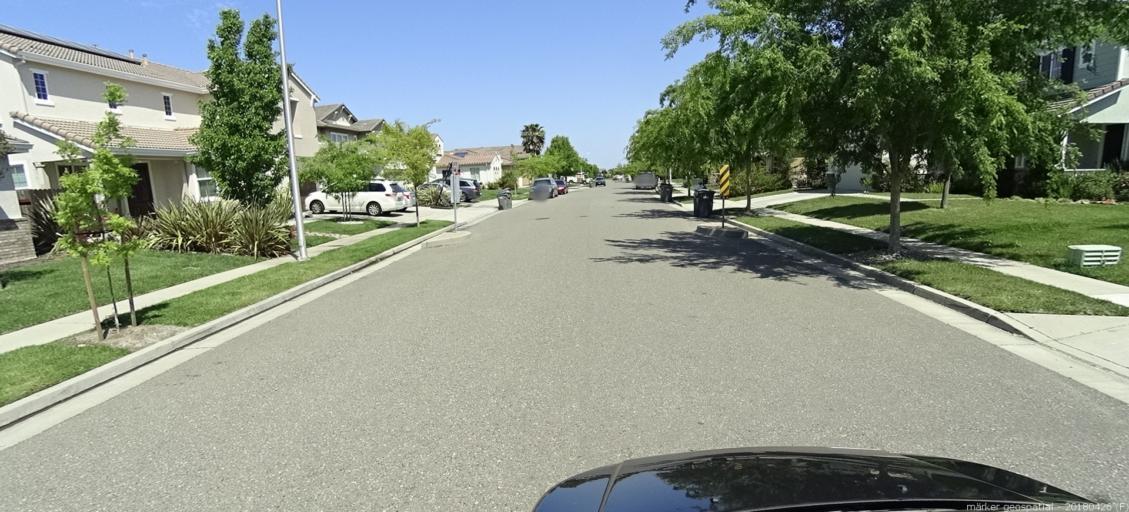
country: US
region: California
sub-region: Yolo County
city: West Sacramento
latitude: 38.5298
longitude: -121.5811
